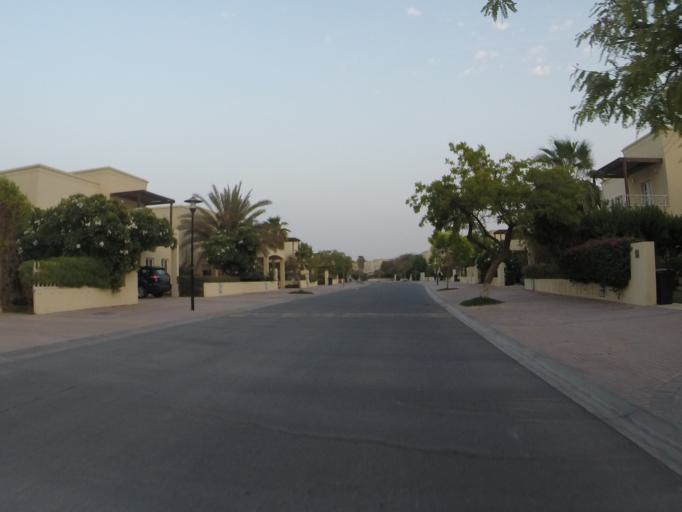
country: AE
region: Dubai
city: Dubai
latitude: 25.0722
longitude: 55.1529
